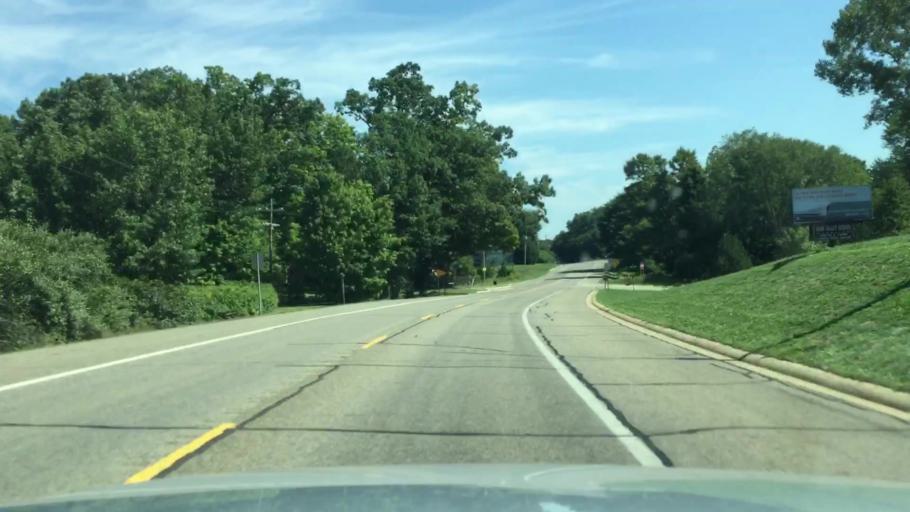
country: US
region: Michigan
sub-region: Jackson County
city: Brooklyn
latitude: 42.0518
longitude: -84.2683
